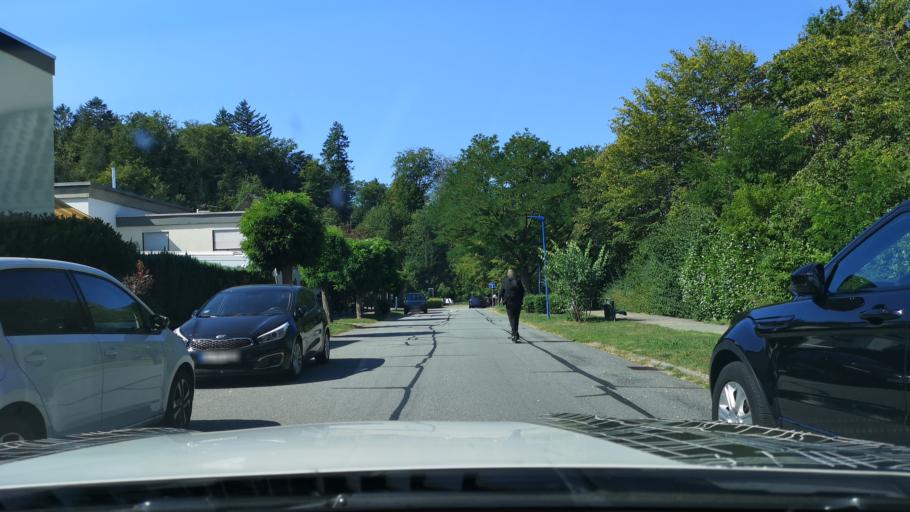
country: DE
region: Baden-Wuerttemberg
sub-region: Karlsruhe Region
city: Ettlingen
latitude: 48.9297
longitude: 8.4614
